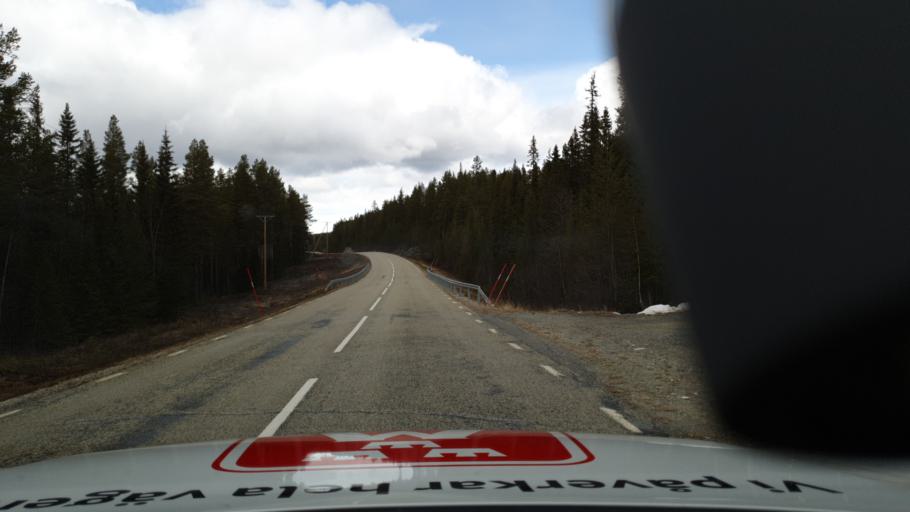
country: SE
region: Jaemtland
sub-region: Are Kommun
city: Jarpen
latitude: 62.7789
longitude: 13.7002
